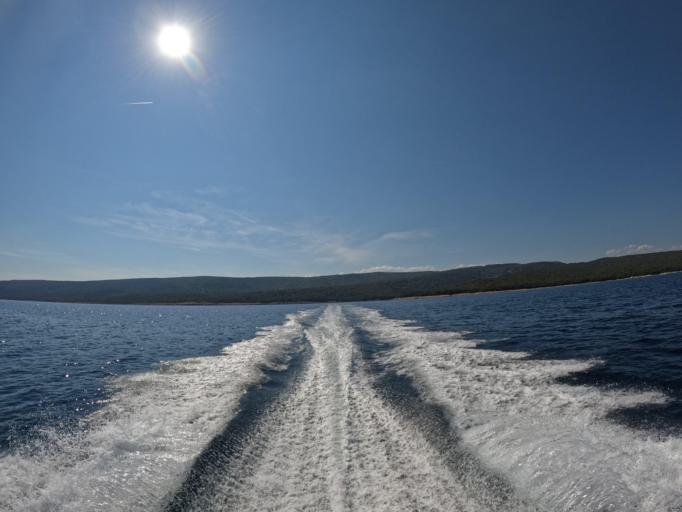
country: HR
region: Primorsko-Goranska
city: Cres
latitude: 44.9459
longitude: 14.4792
